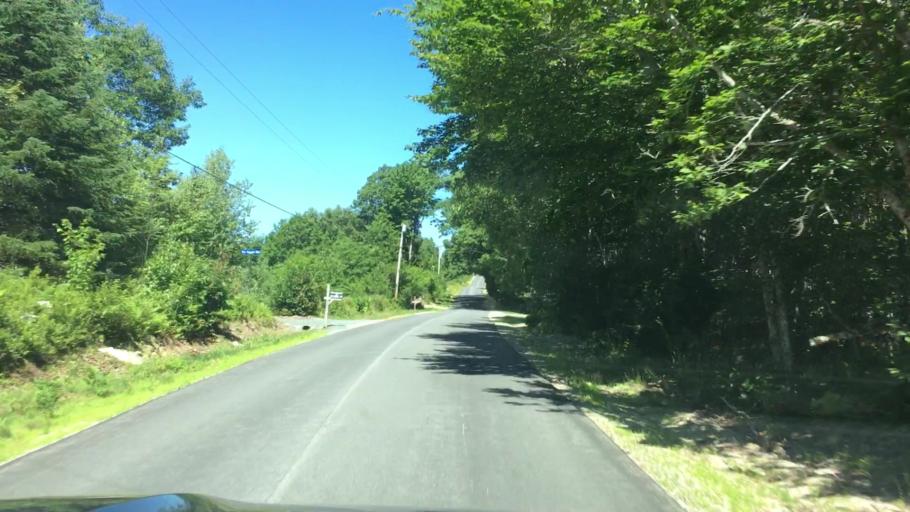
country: US
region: Maine
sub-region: Hancock County
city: Sedgwick
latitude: 44.3204
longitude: -68.6297
